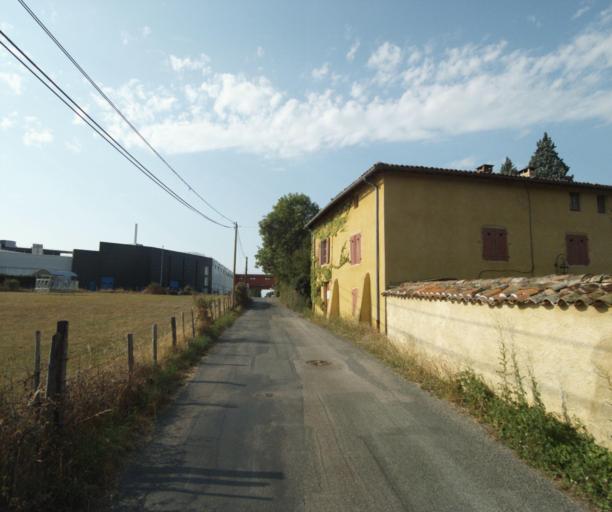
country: FR
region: Rhone-Alpes
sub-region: Departement du Rhone
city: Sain-Bel
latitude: 45.8184
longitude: 4.5921
